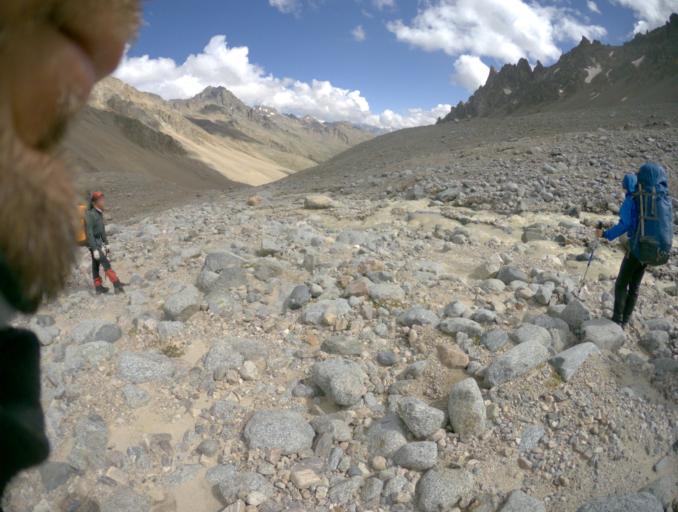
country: RU
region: Kabardino-Balkariya
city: Terskol
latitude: 43.3346
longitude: 42.5505
